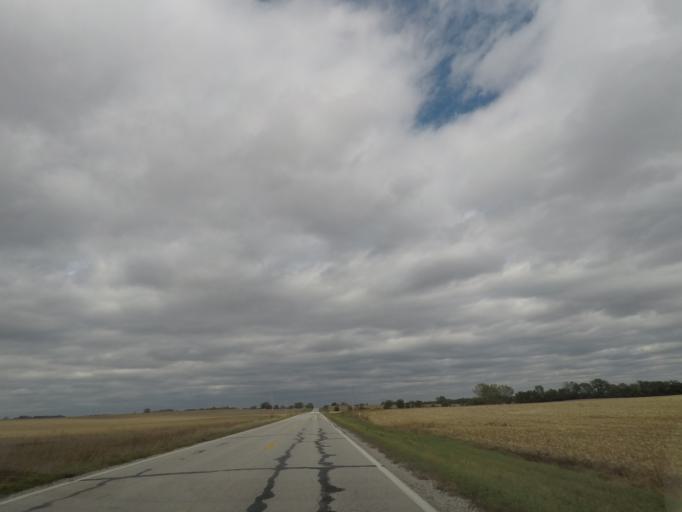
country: US
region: Iowa
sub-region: Story County
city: Huxley
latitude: 41.8534
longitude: -93.5316
